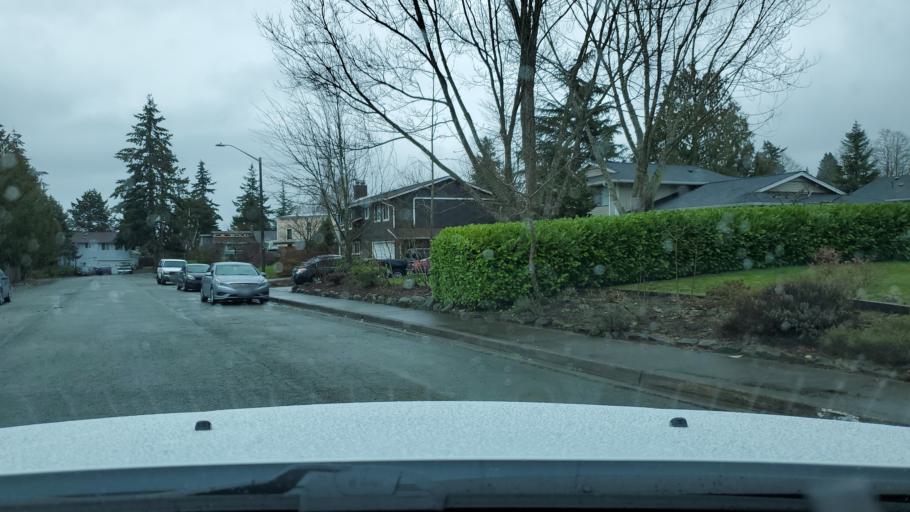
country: US
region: Washington
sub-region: Skagit County
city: Mount Vernon
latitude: 48.4398
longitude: -122.3163
